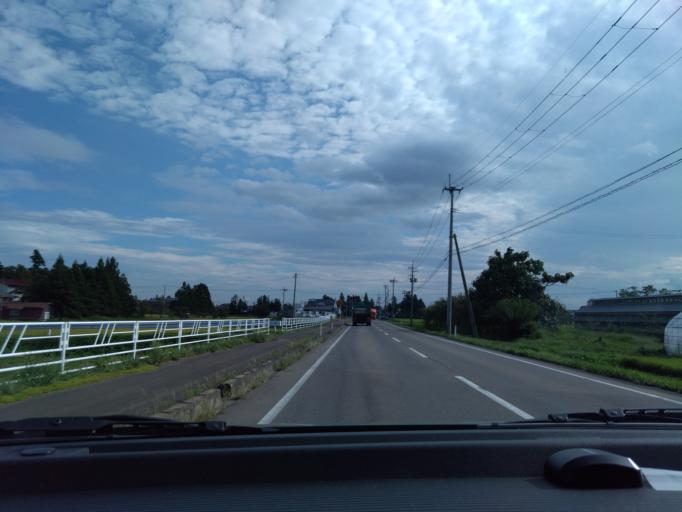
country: JP
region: Iwate
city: Hanamaki
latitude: 39.4489
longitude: 141.0983
